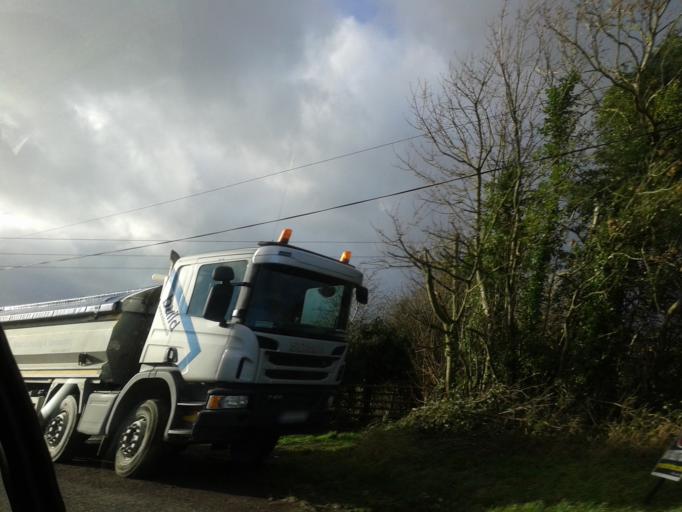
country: IE
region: Leinster
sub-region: An Mhi
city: Slane
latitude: 53.7247
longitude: -6.5223
